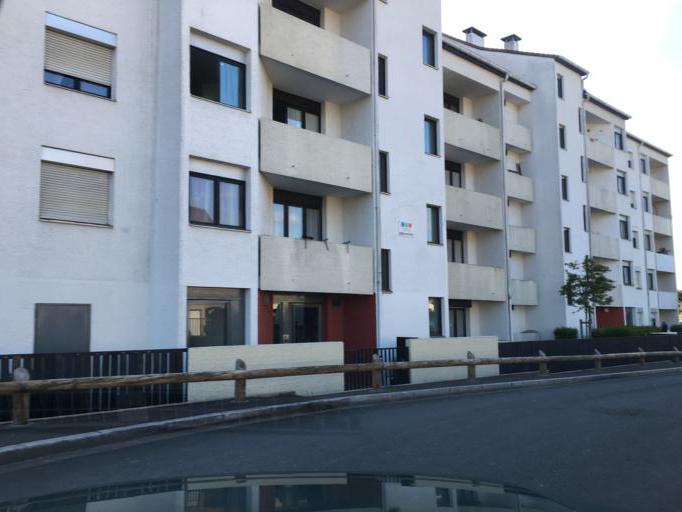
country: FR
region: Centre
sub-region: Departement du Loiret
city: Fleury-les-Aubrais
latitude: 47.9321
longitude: 1.9072
